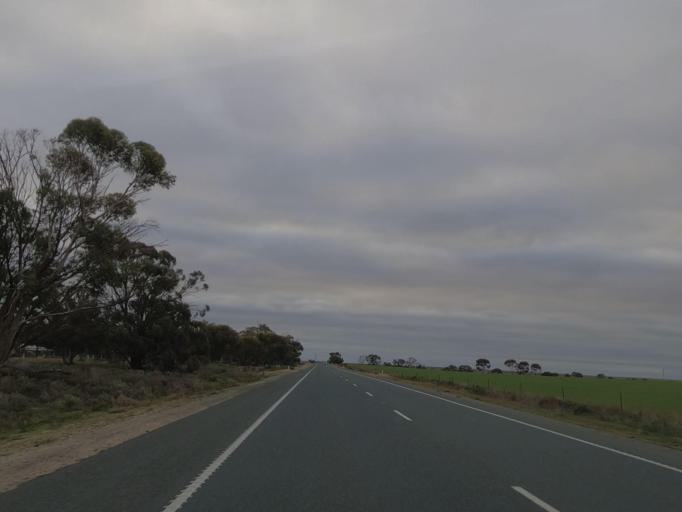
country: AU
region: Victoria
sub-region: Swan Hill
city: Swan Hill
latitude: -35.5590
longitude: 143.7798
